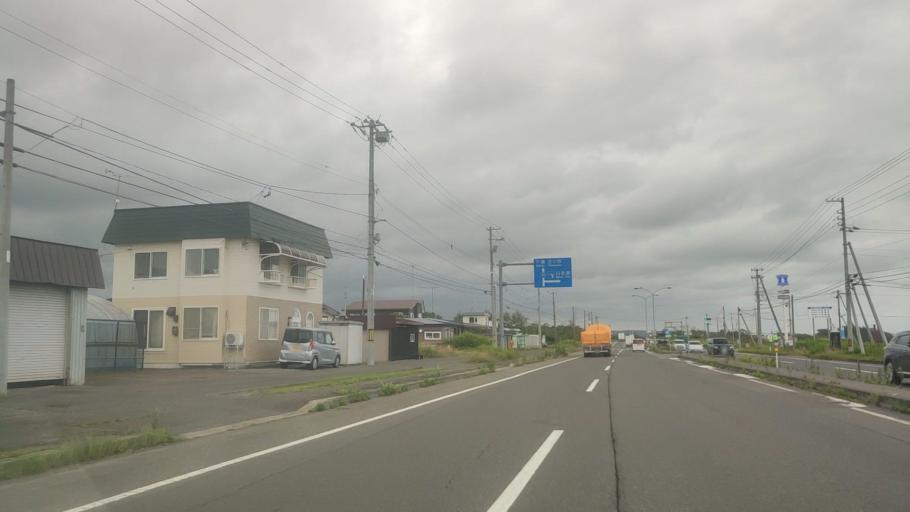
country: JP
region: Hokkaido
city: Shiraoi
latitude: 42.5283
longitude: 141.3210
